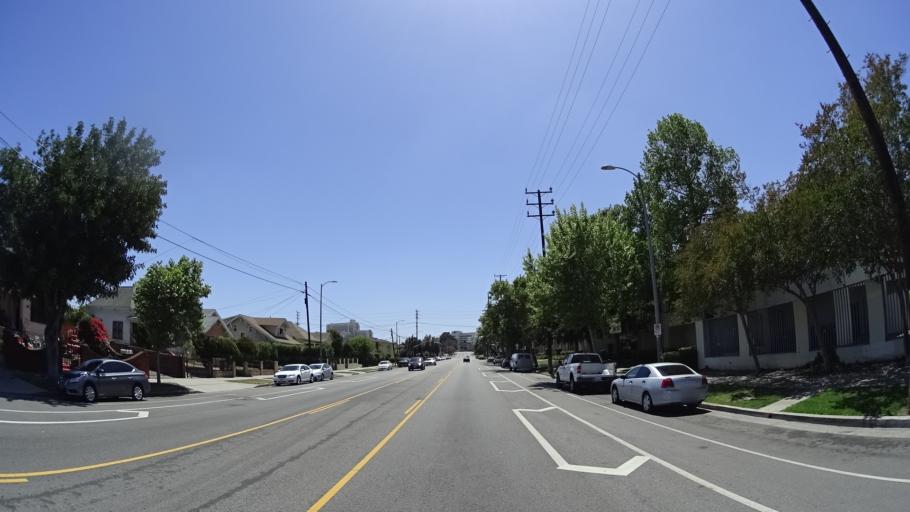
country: US
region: California
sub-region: Los Angeles County
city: Boyle Heights
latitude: 34.0690
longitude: -118.2116
